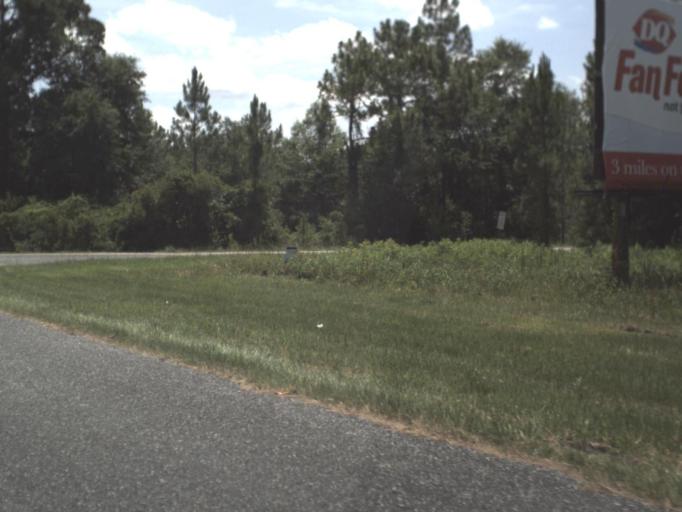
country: US
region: Florida
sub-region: Dixie County
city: Cross City
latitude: 29.6538
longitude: -83.1761
